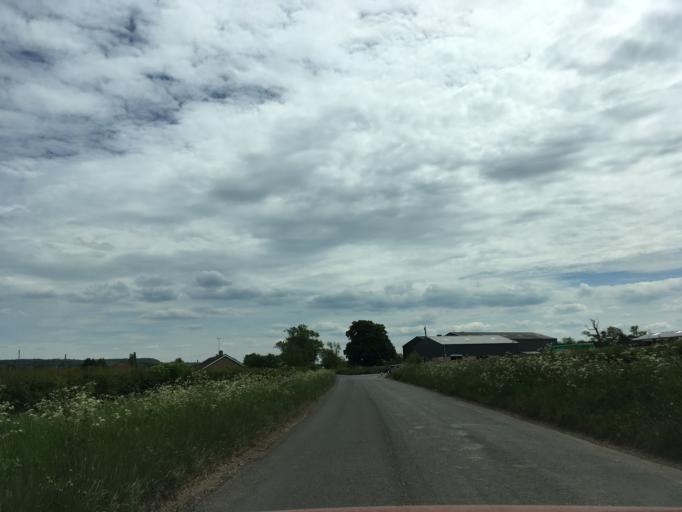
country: GB
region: England
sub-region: Gloucestershire
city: Berkeley
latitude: 51.6761
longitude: -2.4246
